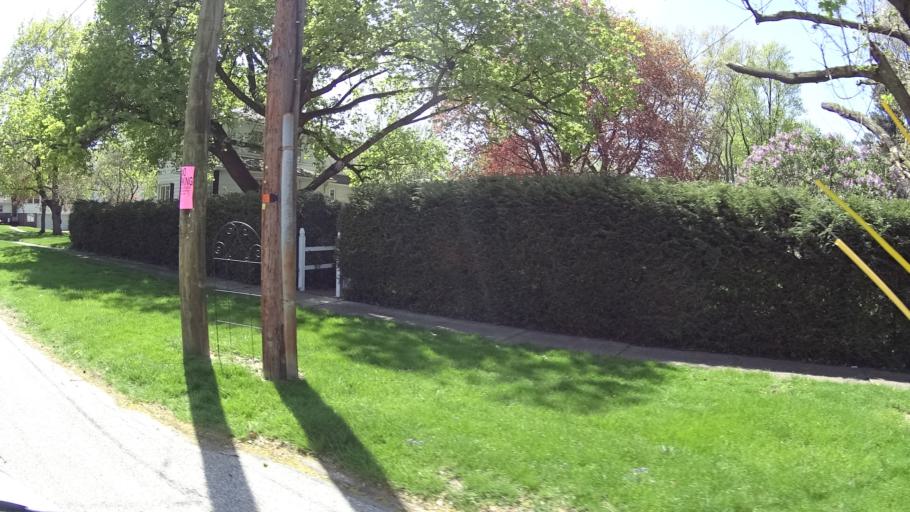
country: US
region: Ohio
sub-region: Lorain County
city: Elyria
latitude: 41.3766
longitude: -82.0999
